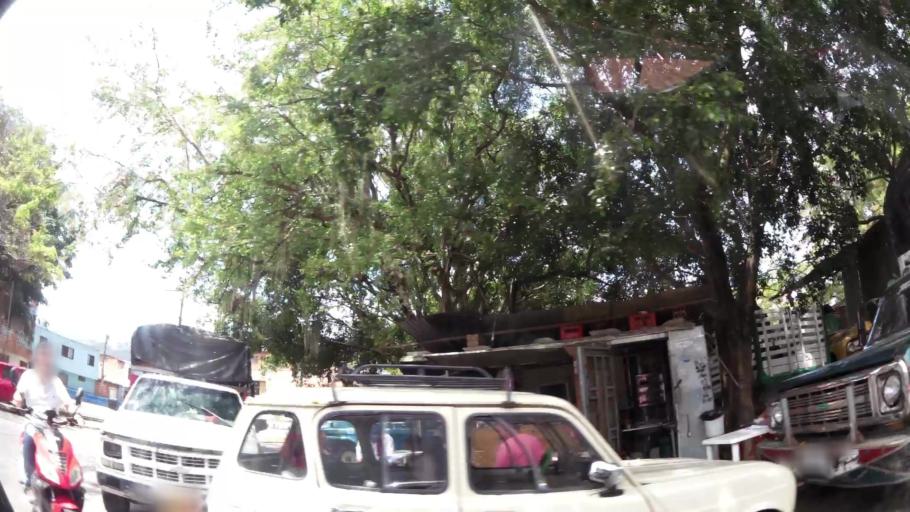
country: CO
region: Antioquia
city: Bello
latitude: 6.3392
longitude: -75.5534
